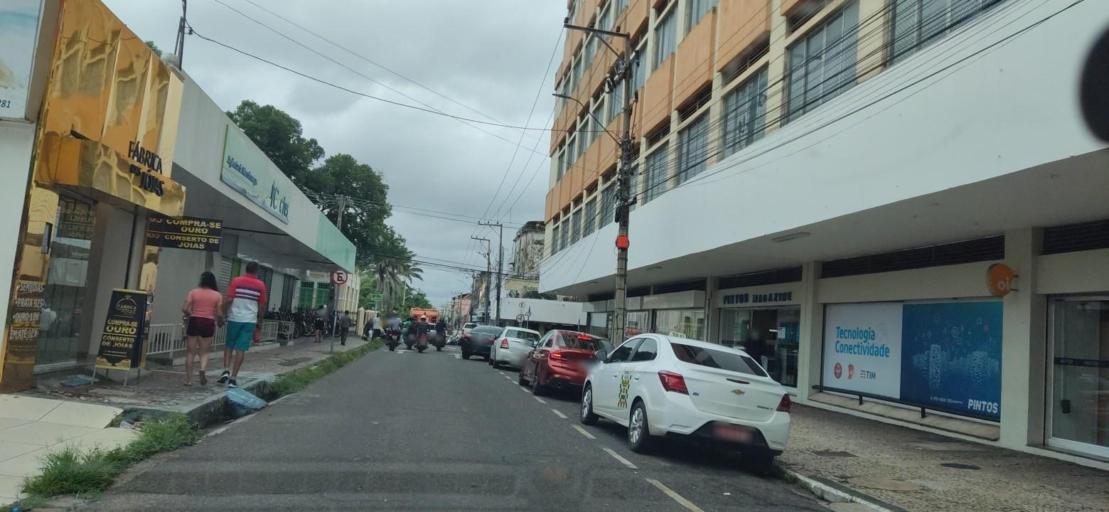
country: BR
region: Piaui
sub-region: Teresina
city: Teresina
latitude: -5.0900
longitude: -42.8142
